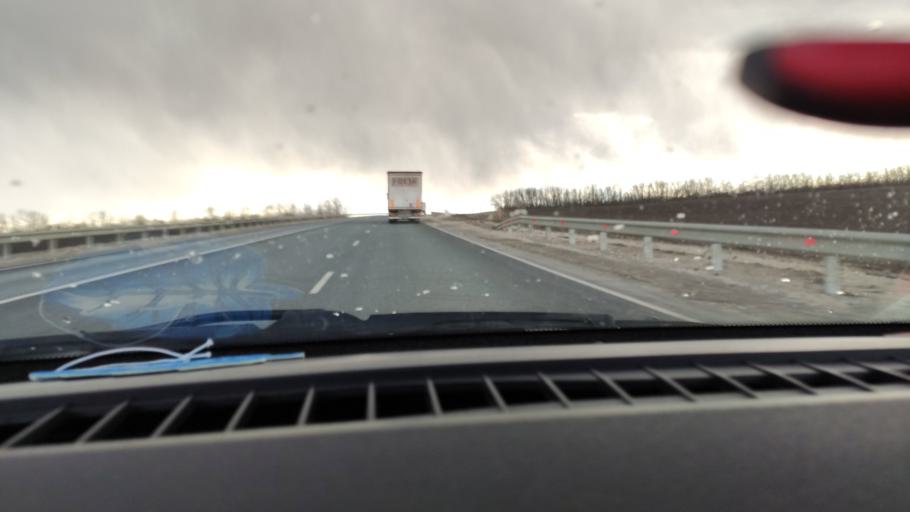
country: RU
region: Saratov
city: Yelshanka
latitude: 51.8349
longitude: 46.4691
